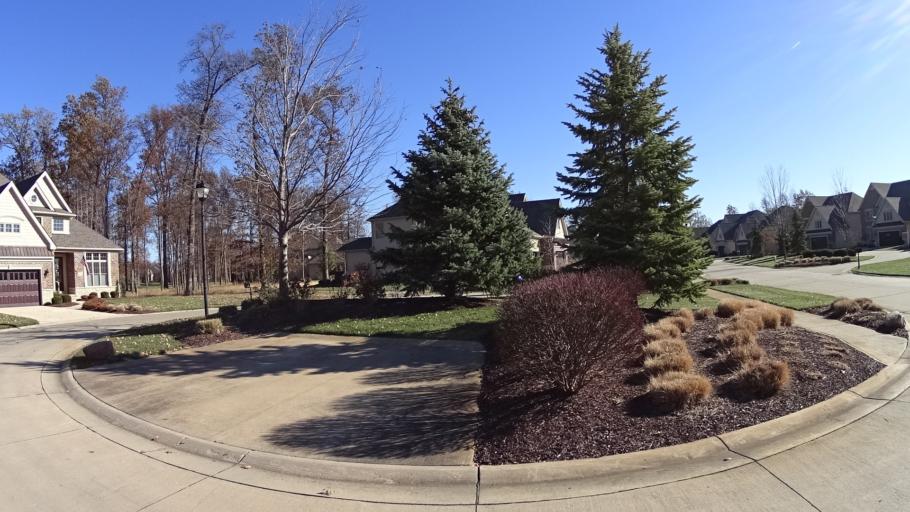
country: US
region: Ohio
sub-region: Lorain County
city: Avon Lake
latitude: 41.4853
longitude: -82.0117
